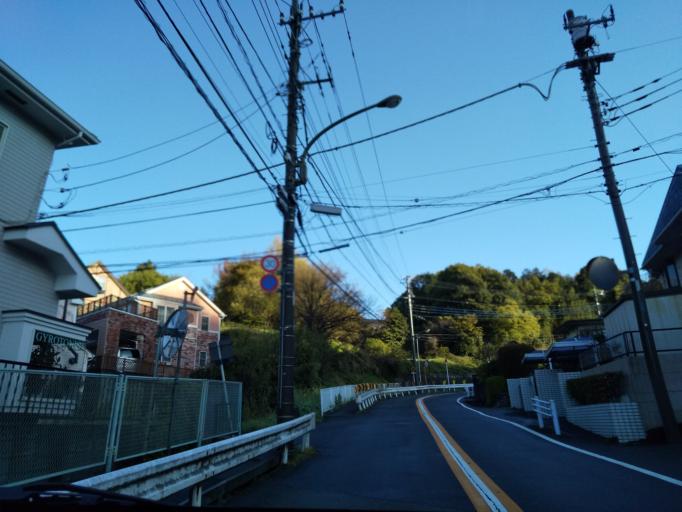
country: JP
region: Tokyo
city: Hachioji
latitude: 35.6299
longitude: 139.3620
